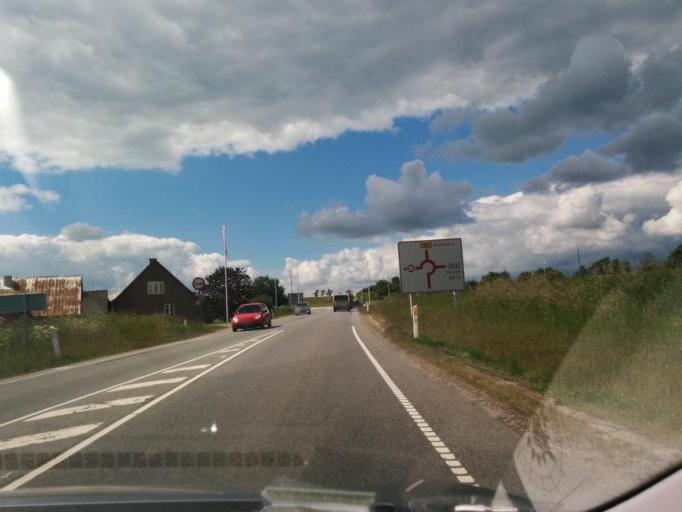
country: DK
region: Central Jutland
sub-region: Syddjurs Kommune
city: Ronde
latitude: 56.3156
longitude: 10.4267
